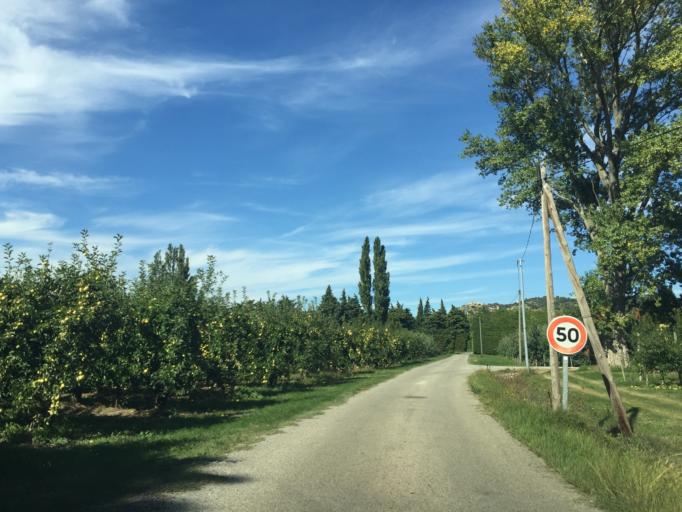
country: FR
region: Provence-Alpes-Cote d'Azur
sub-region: Departement du Vaucluse
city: Mornas
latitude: 44.1916
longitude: 4.7304
